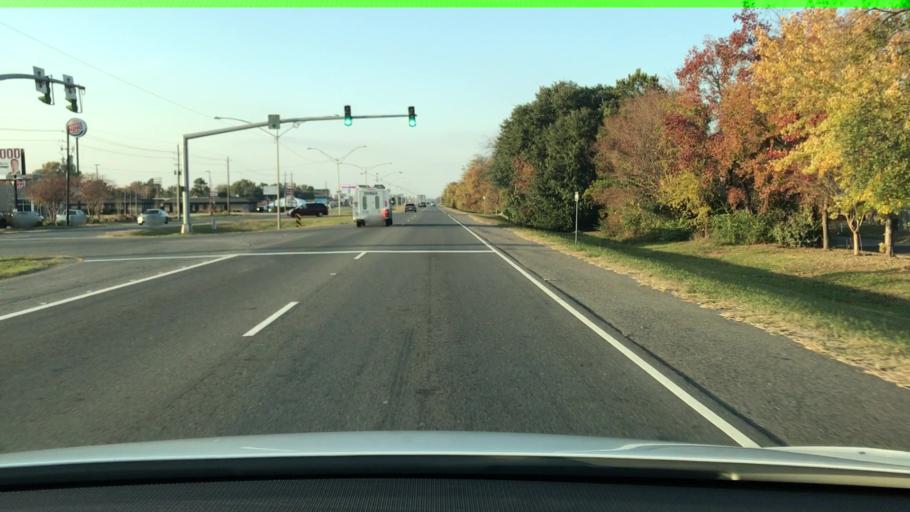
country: US
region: Louisiana
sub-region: Bossier Parish
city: Bossier City
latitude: 32.4200
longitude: -93.7049
